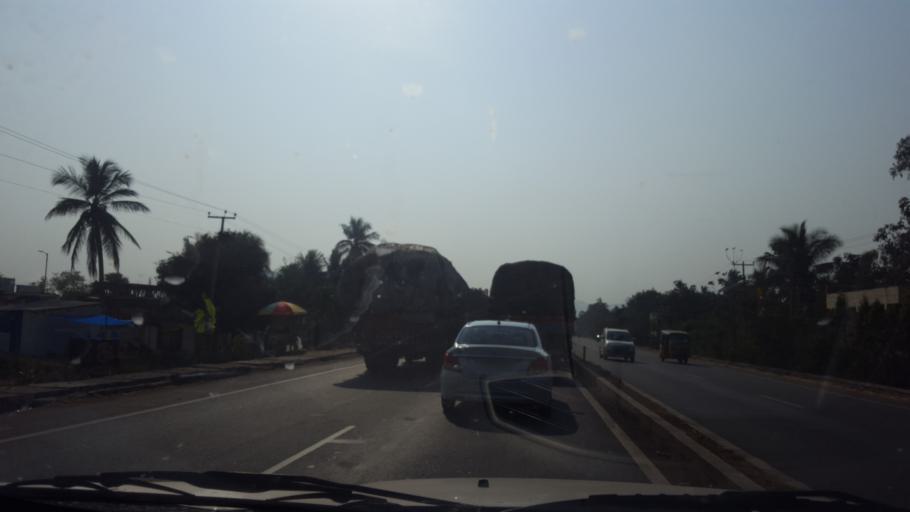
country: IN
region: Andhra Pradesh
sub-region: Vishakhapatnam
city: Anakapalle
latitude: 17.6671
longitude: 82.9585
